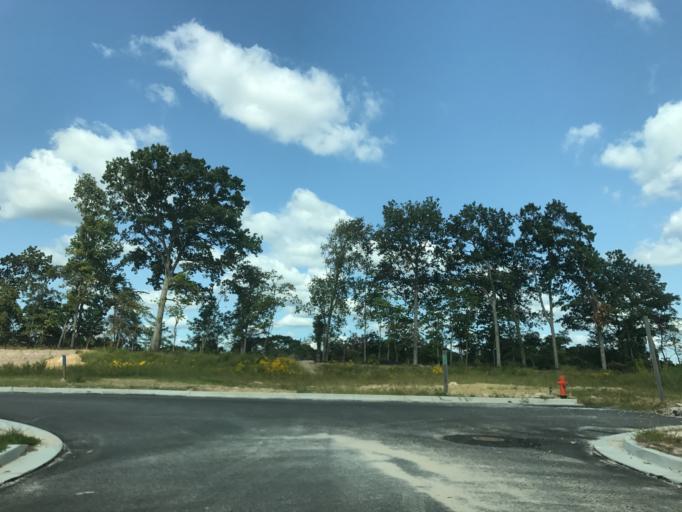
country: US
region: Maryland
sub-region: Baltimore County
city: Bowleys Quarters
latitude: 39.3611
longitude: -76.3998
